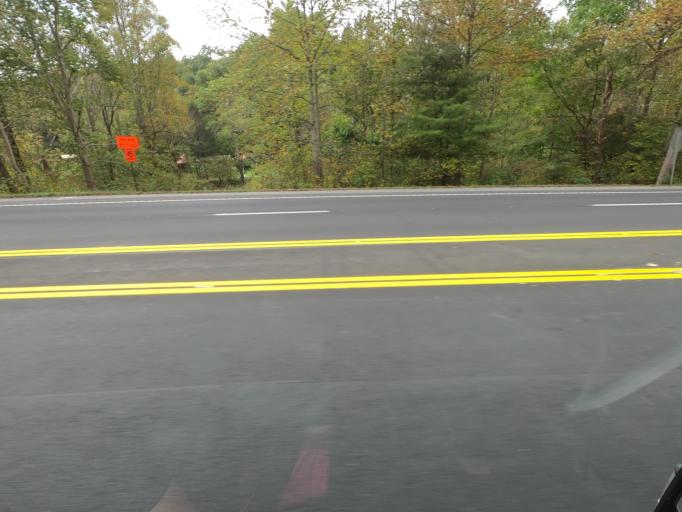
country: US
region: Tennessee
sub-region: Carter County
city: Elizabethton
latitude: 36.2413
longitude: -82.1885
